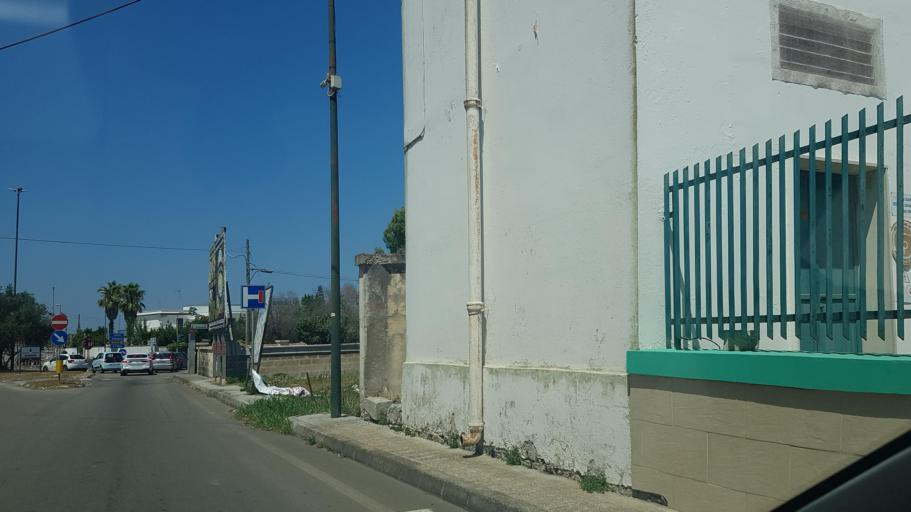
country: IT
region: Apulia
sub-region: Provincia di Lecce
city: Melendugno
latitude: 40.2785
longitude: 18.3442
